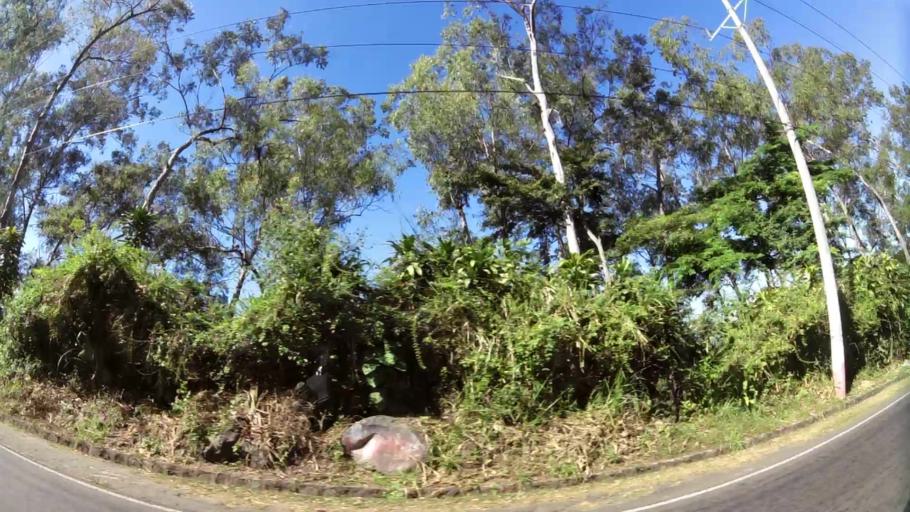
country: SV
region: Ahuachapan
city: Ahuachapan
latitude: 13.9071
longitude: -89.8331
